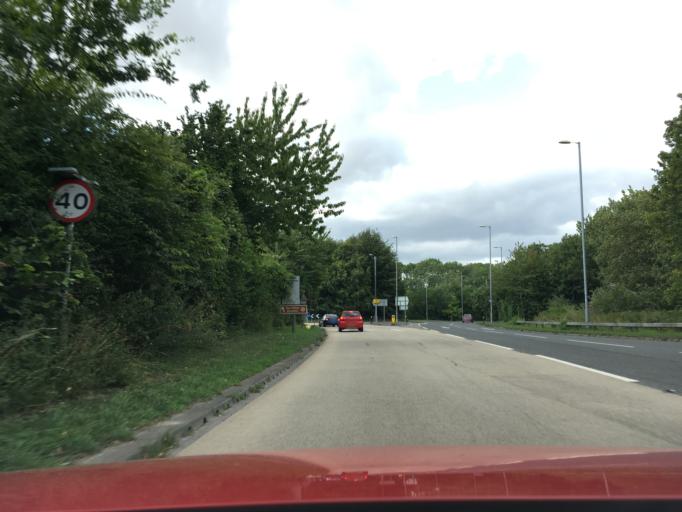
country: GB
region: England
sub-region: Hampshire
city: Compton
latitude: 51.0373
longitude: -1.3273
